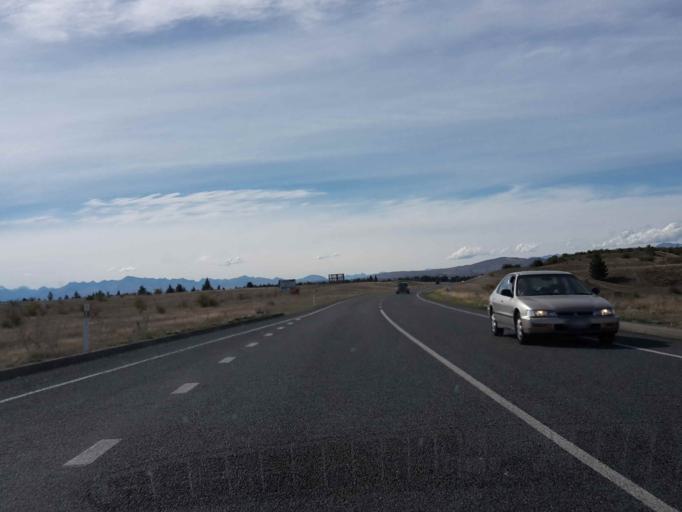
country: NZ
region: Otago
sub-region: Queenstown-Lakes District
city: Wanaka
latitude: -44.2827
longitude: 170.0896
